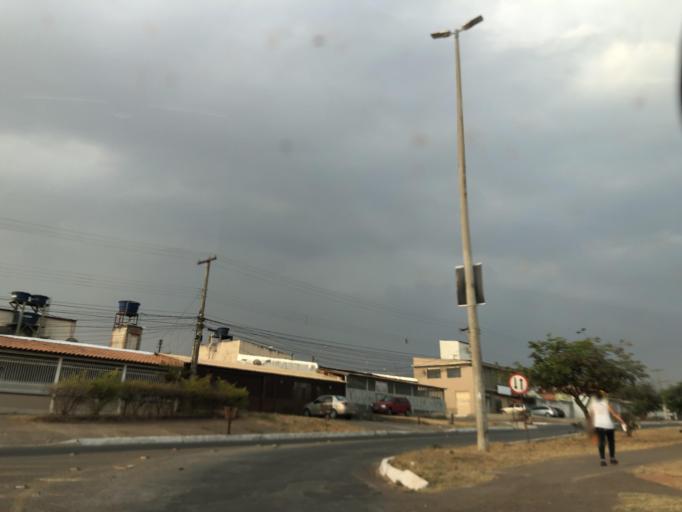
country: BR
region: Federal District
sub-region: Brasilia
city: Brasilia
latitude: -15.9147
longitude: -48.0615
